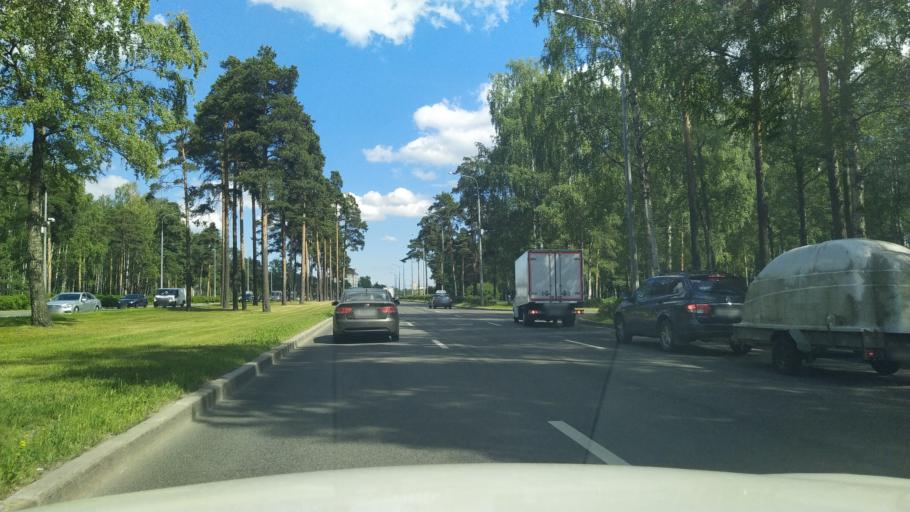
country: RU
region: Leningrad
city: Kalininskiy
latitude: 59.9947
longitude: 30.4008
